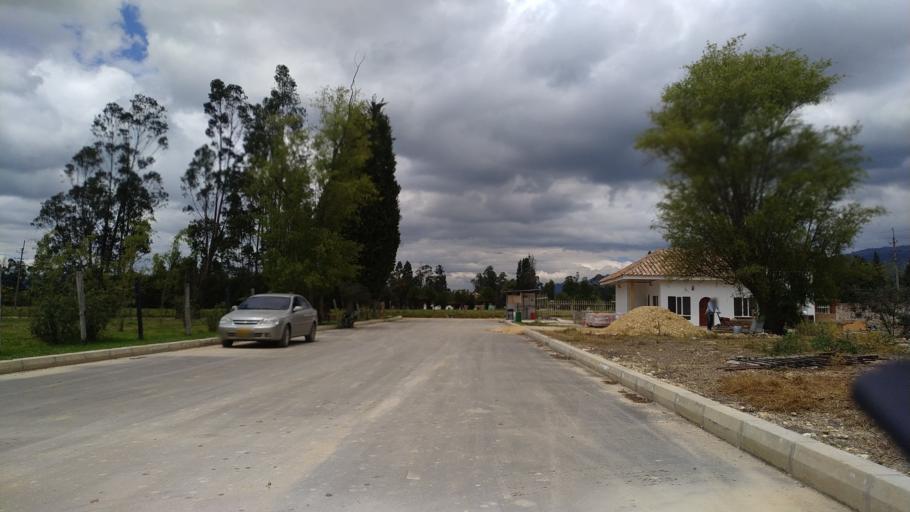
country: CO
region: Boyaca
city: Duitama
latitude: 5.7960
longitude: -73.0695
